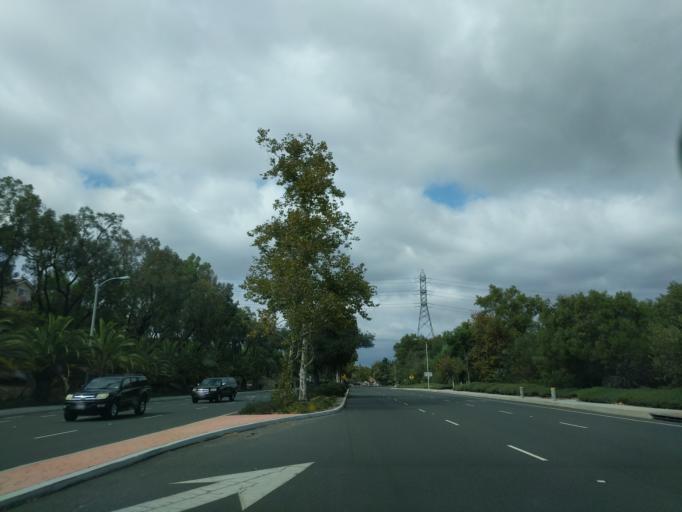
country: US
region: California
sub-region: Orange County
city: Laguna Woods
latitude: 33.5960
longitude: -117.7487
